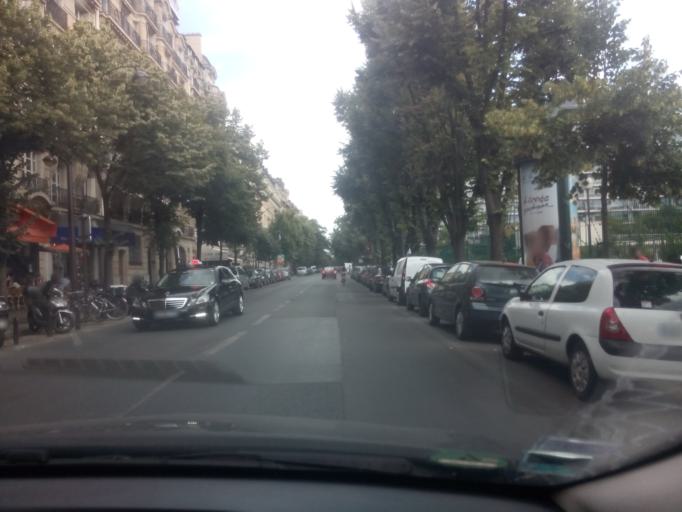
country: FR
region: Ile-de-France
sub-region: Departement des Hauts-de-Seine
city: Vanves
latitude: 48.8568
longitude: 2.2921
